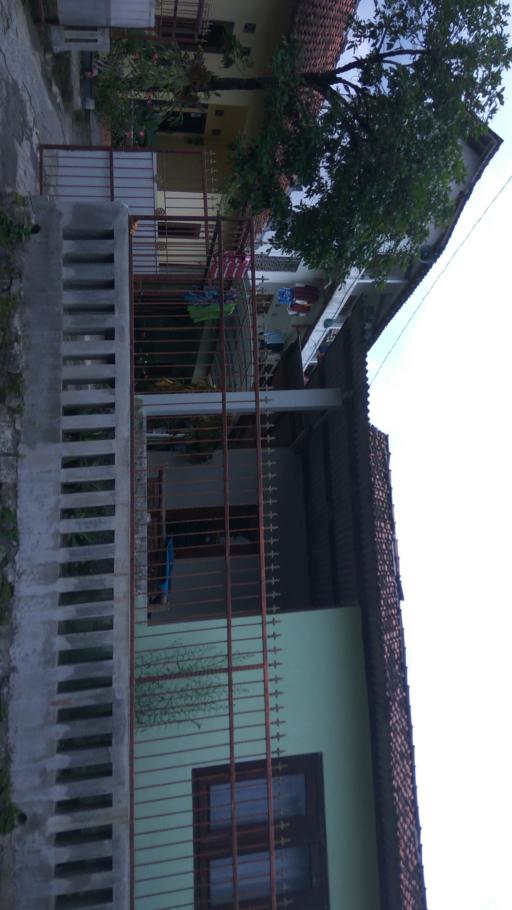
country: ID
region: Daerah Istimewa Yogyakarta
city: Melati
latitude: -7.7343
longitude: 110.4031
